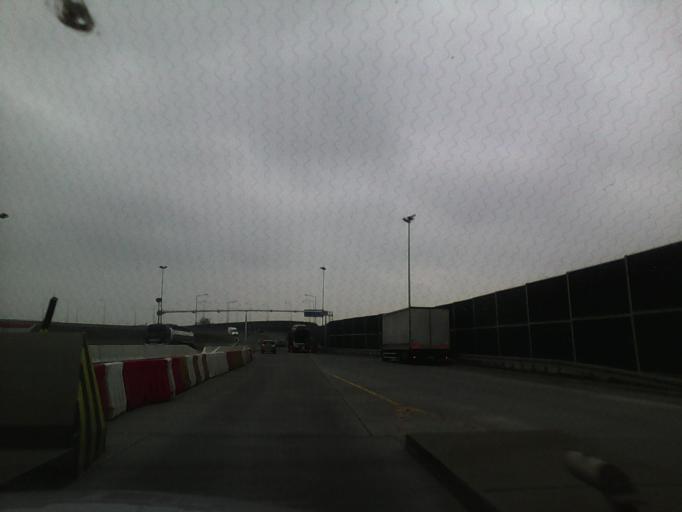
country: PL
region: Masovian Voivodeship
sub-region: Powiat zyrardowski
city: Wiskitki
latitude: 52.0896
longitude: 20.3595
